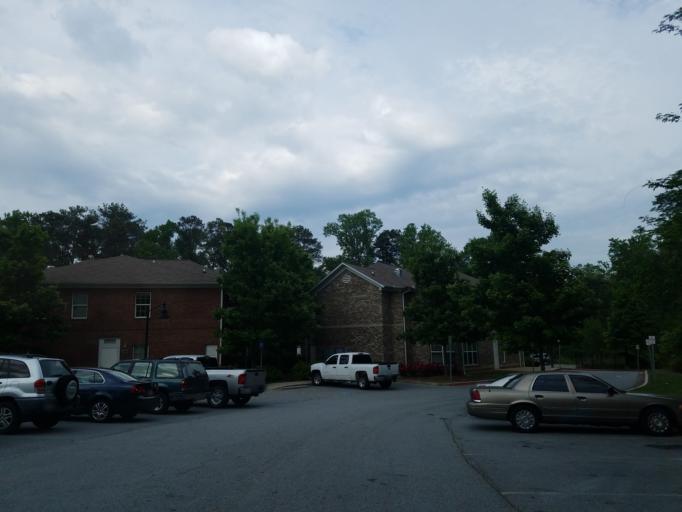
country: US
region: Georgia
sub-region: Cobb County
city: Fair Oaks
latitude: 33.9350
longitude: -84.5254
